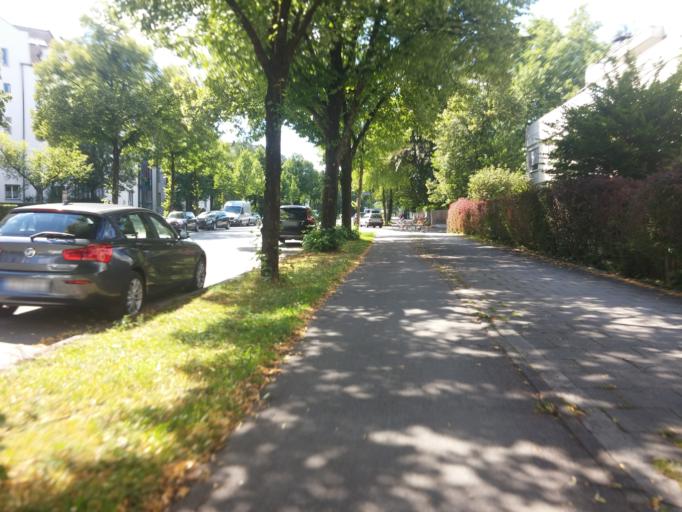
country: DE
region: Bavaria
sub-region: Upper Bavaria
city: Bogenhausen
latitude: 48.1470
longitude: 11.6312
